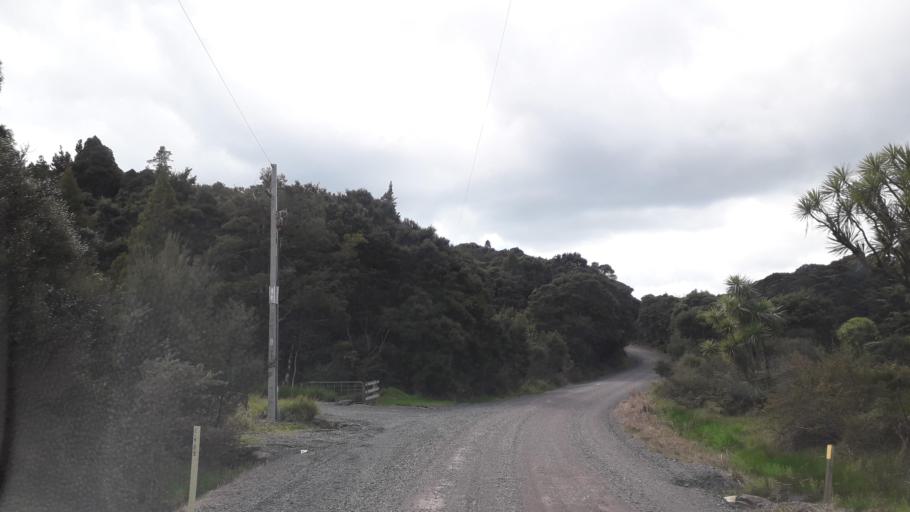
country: NZ
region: Northland
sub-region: Far North District
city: Paihia
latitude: -35.3062
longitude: 174.2200
